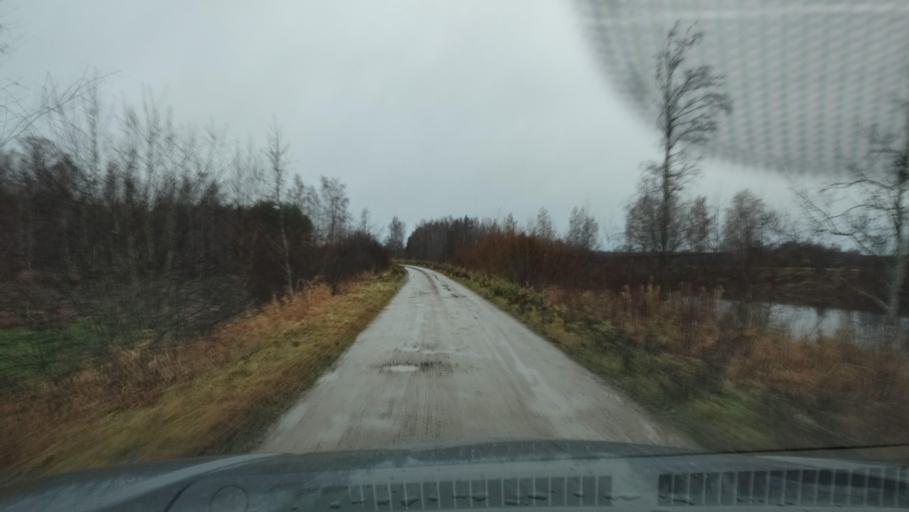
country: FI
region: Ostrobothnia
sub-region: Sydosterbotten
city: Kristinestad
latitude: 62.2359
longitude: 21.4611
